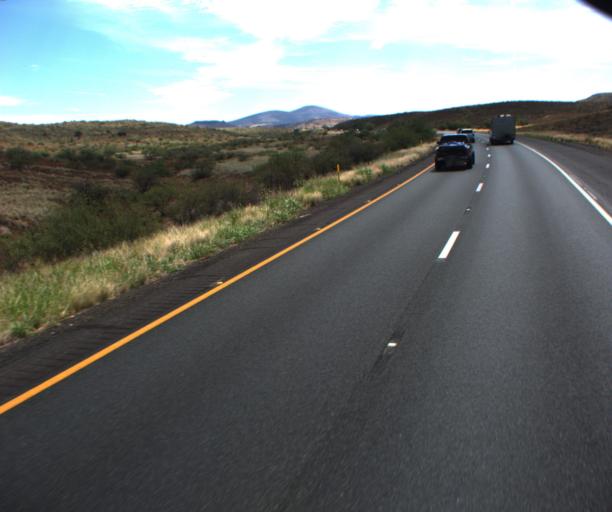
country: US
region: Arizona
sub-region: Yavapai County
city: Cordes Lakes
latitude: 34.4215
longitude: -112.0532
